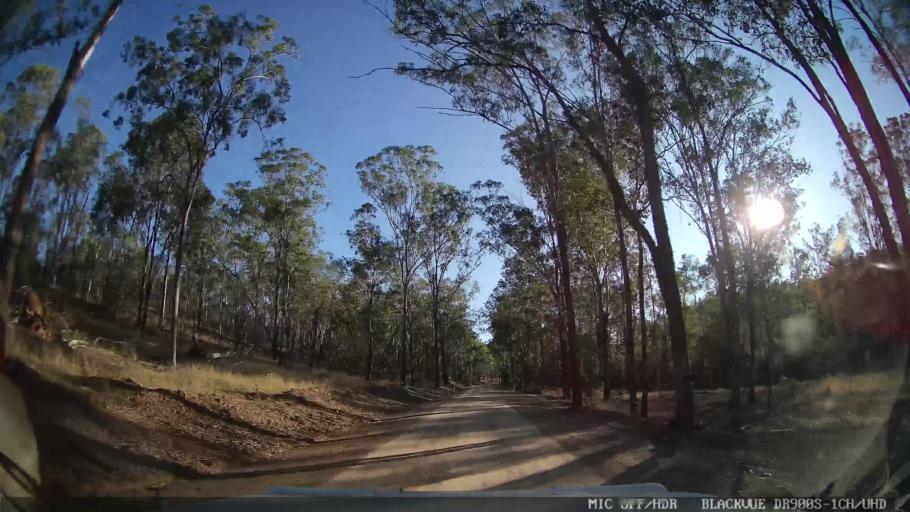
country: AU
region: Queensland
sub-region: Gladstone
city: Toolooa
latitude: -24.6949
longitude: 151.4113
